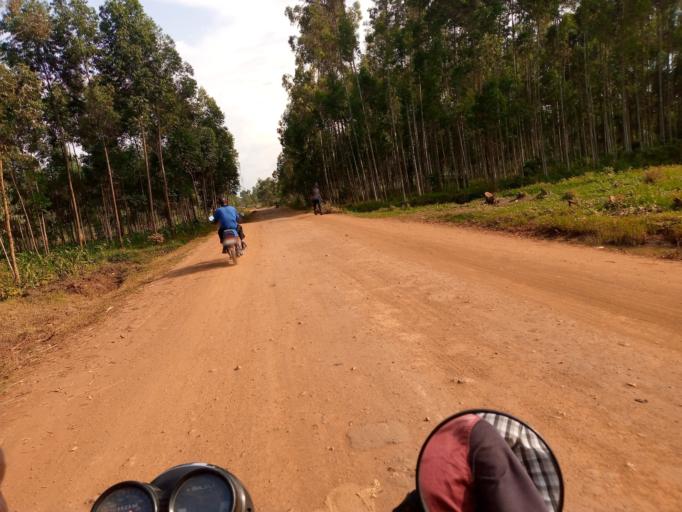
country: UG
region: Eastern Region
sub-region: Mbale District
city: Mbale
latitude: 1.0677
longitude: 34.1558
